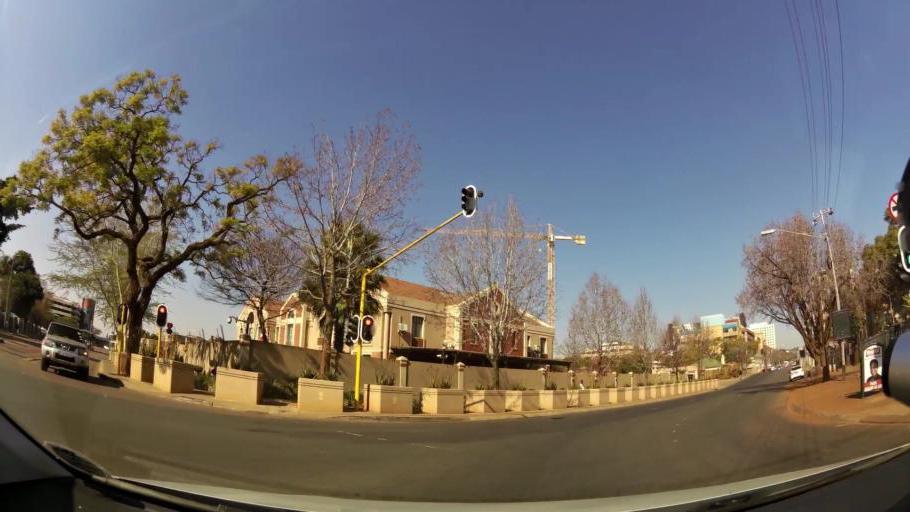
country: ZA
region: Gauteng
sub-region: City of Tshwane Metropolitan Municipality
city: Pretoria
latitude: -25.7477
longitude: 28.2348
